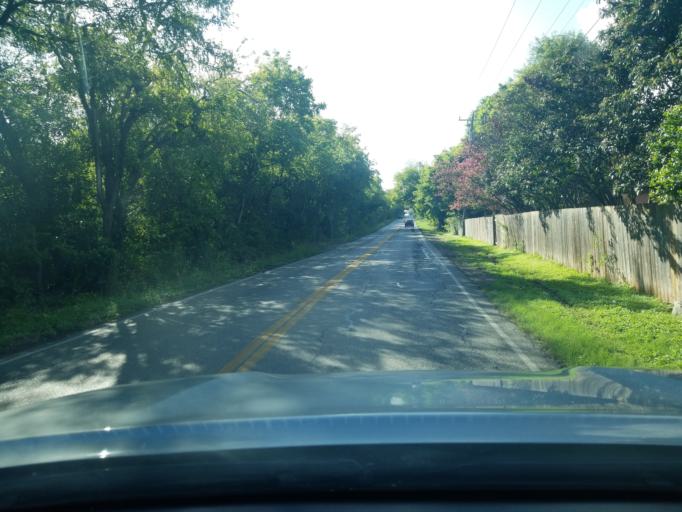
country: US
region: Texas
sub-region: Bexar County
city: Live Oak
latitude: 29.5957
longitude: -98.3602
